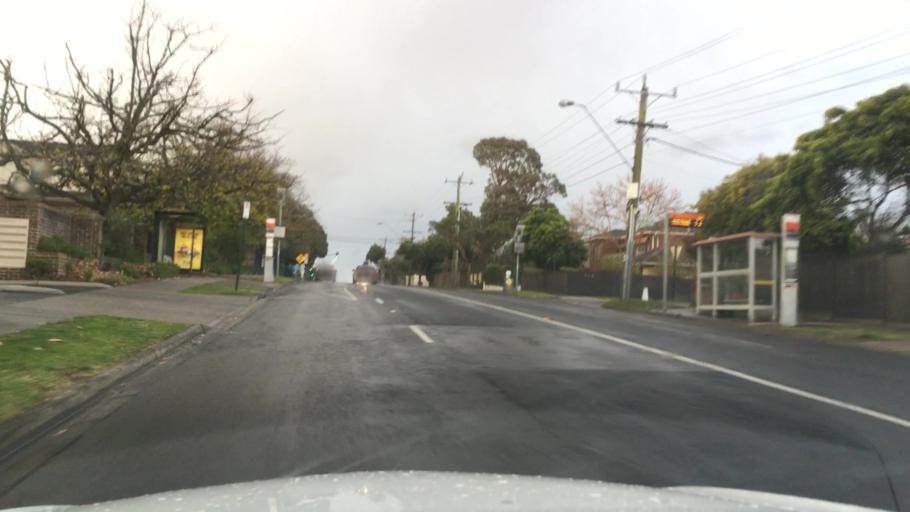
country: AU
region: Victoria
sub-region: Whitehorse
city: Box Hill South
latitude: -37.8342
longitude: 145.1208
